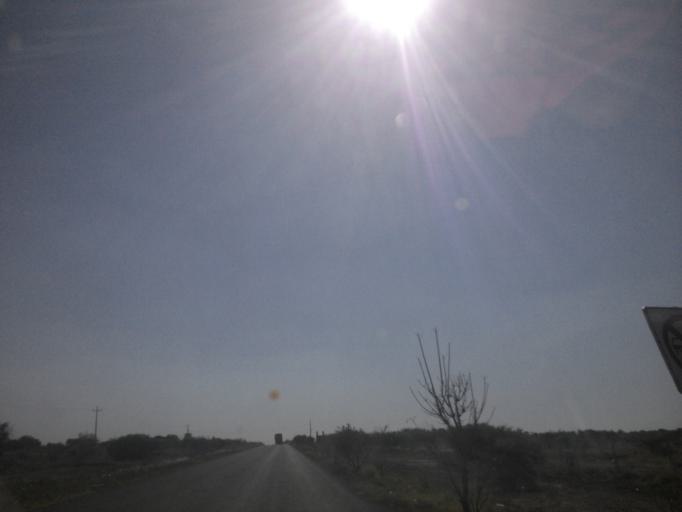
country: MX
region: Jalisco
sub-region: Arandas
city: Santiaguito (Santiaguito de Velazquez)
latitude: 20.8226
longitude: -102.1812
